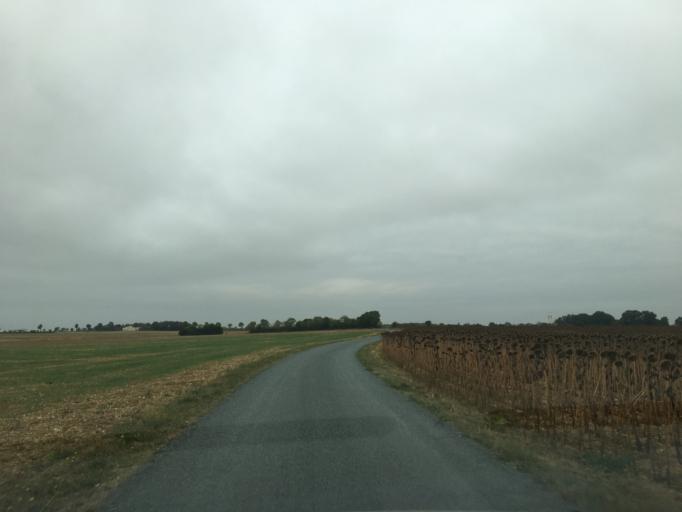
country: FR
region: Poitou-Charentes
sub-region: Departement des Deux-Sevres
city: Beauvoir-sur-Niort
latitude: 46.0855
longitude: -0.4947
